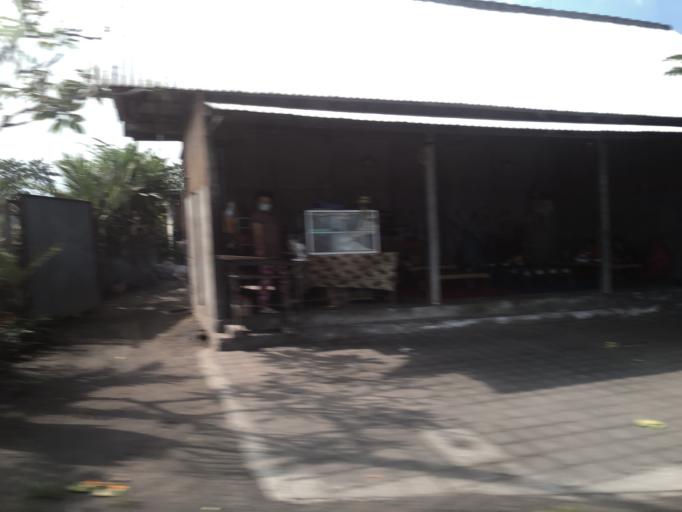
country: ID
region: Bali
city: Banjar Bucu
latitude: -8.5758
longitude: 115.1976
